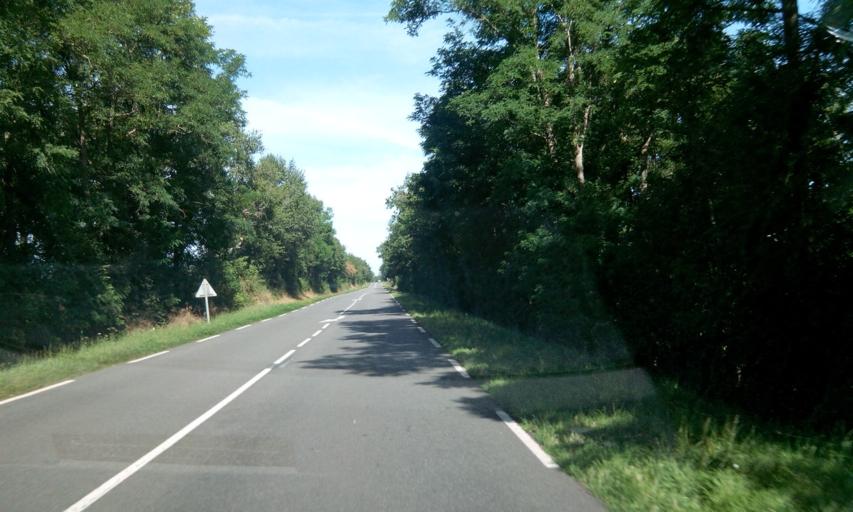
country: FR
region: Poitou-Charentes
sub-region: Departement de la Charente
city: Chabanais
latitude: 45.9469
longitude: 0.7224
